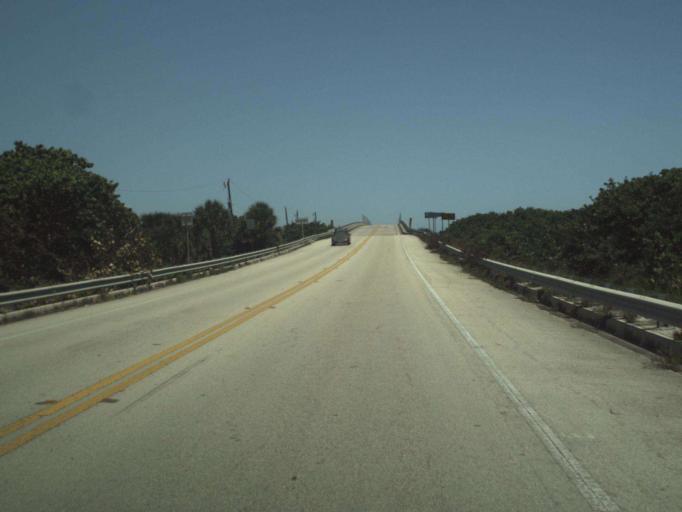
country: US
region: Florida
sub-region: Indian River County
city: Sebastian
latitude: 27.8572
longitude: -80.4469
